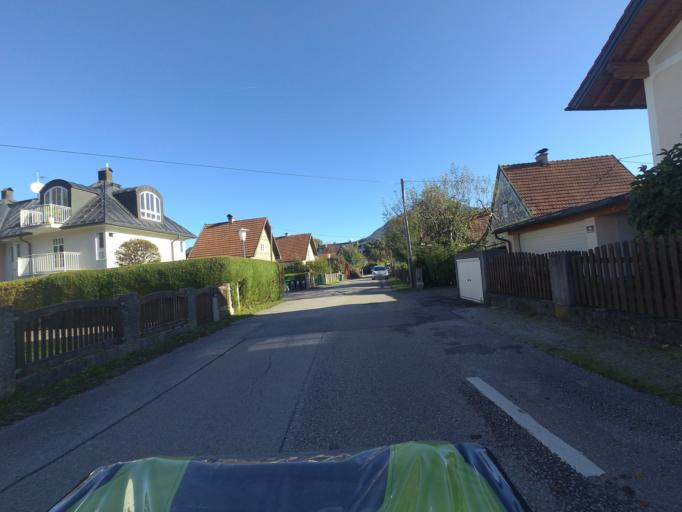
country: AT
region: Salzburg
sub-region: Salzburg Stadt
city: Salzburg
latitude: 47.7818
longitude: 13.0629
